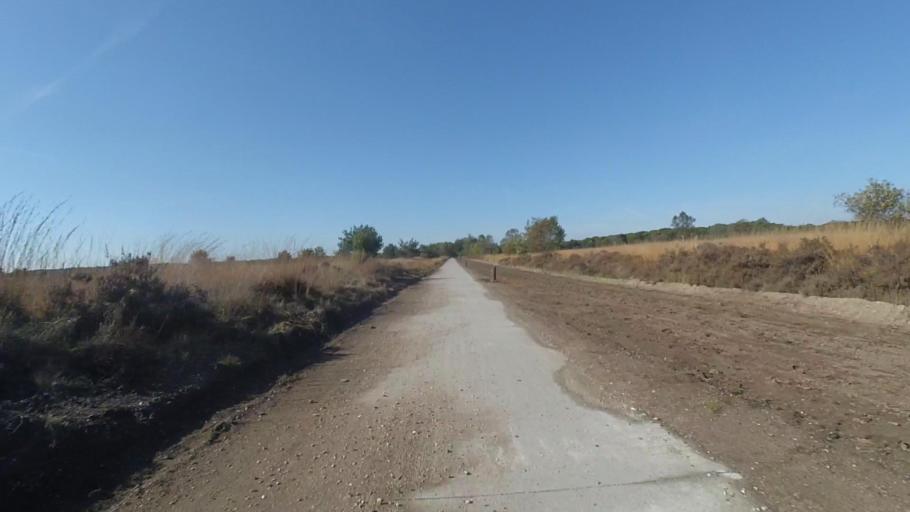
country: NL
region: Gelderland
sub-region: Gemeente Barneveld
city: Stroe
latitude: 52.1868
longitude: 5.7210
